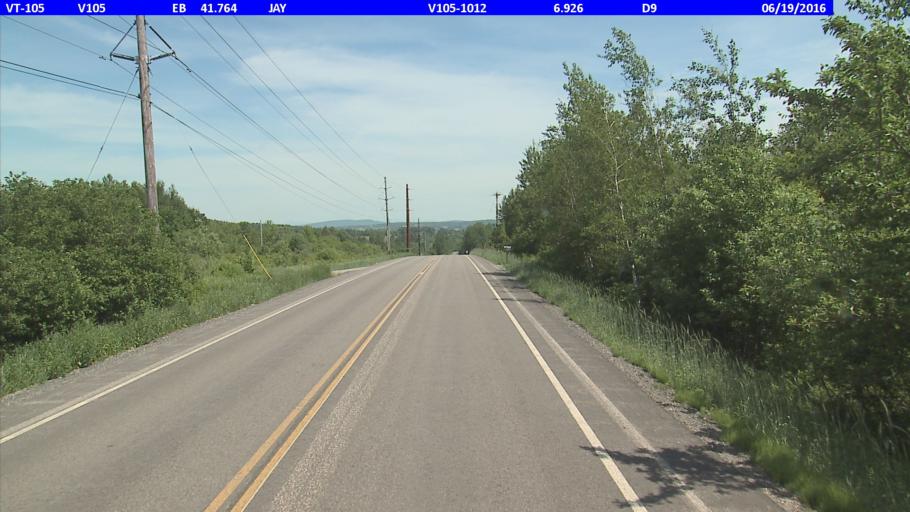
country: CA
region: Quebec
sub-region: Monteregie
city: Sutton
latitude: 44.9703
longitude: -72.4499
